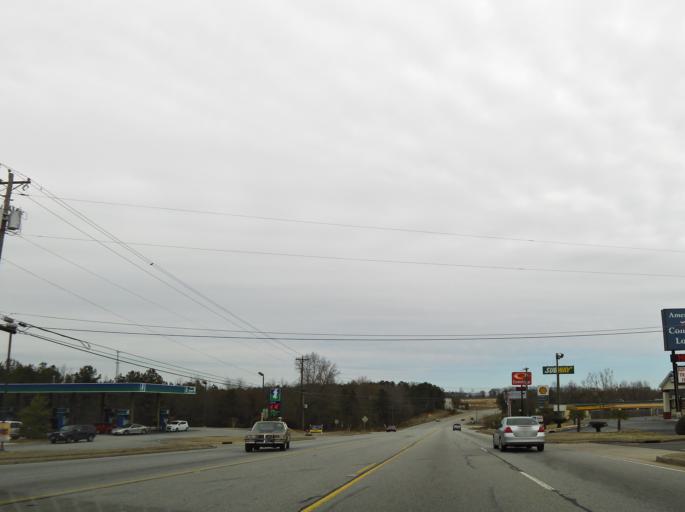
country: US
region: Georgia
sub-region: Peach County
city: Byron
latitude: 32.6133
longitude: -83.7415
